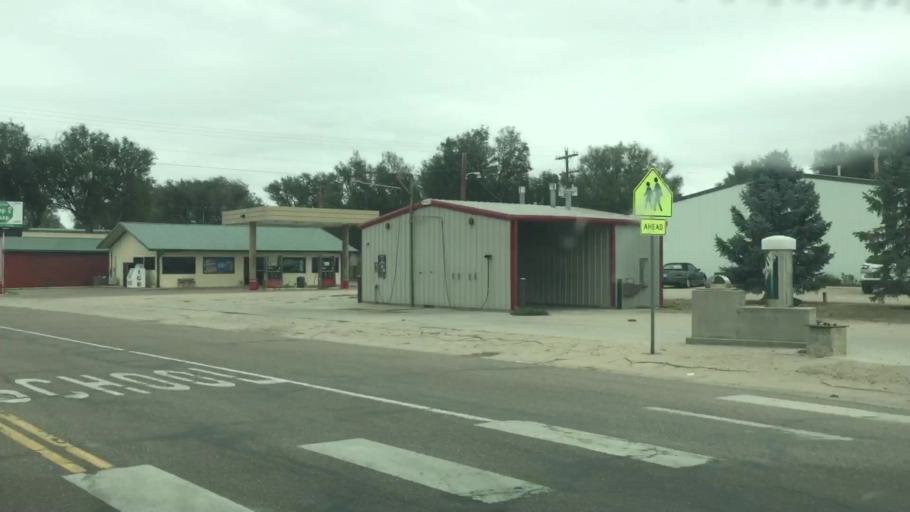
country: US
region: Colorado
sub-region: Prowers County
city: Lamar
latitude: 38.0627
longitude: -102.3103
